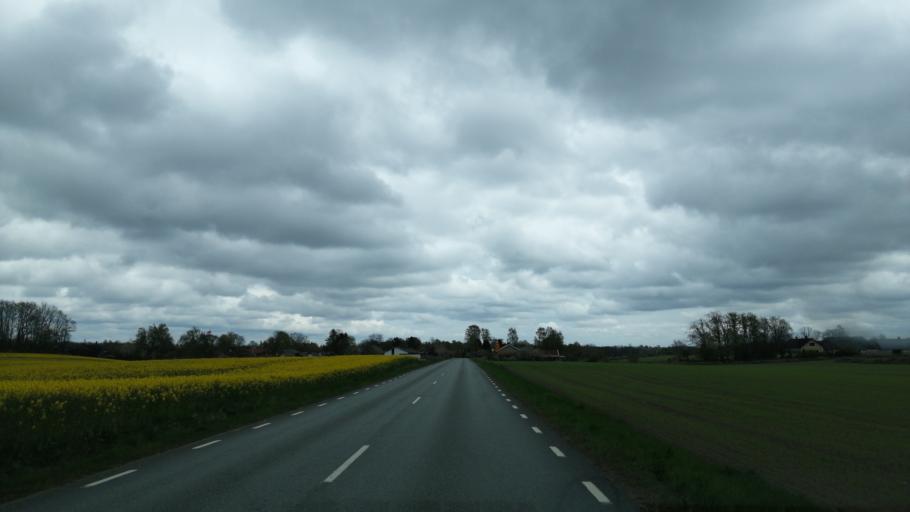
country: SE
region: Skane
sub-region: Kristianstads Kommun
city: Onnestad
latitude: 55.9931
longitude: 14.0264
